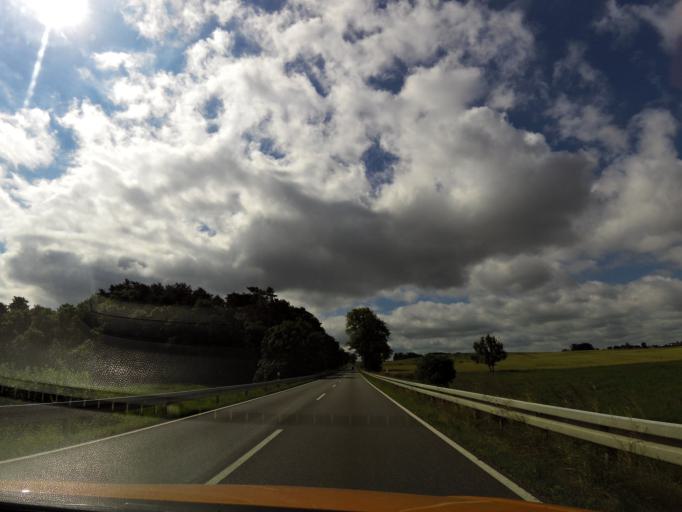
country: DE
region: Mecklenburg-Vorpommern
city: Krakow am See
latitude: 53.7087
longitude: 12.2775
